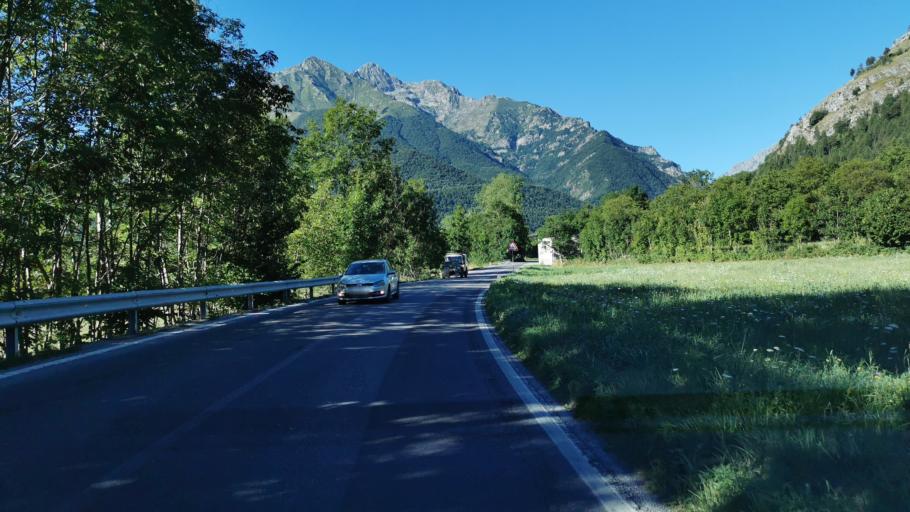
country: IT
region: Piedmont
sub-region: Provincia di Cuneo
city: Valdieri
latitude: 44.2684
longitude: 7.3886
